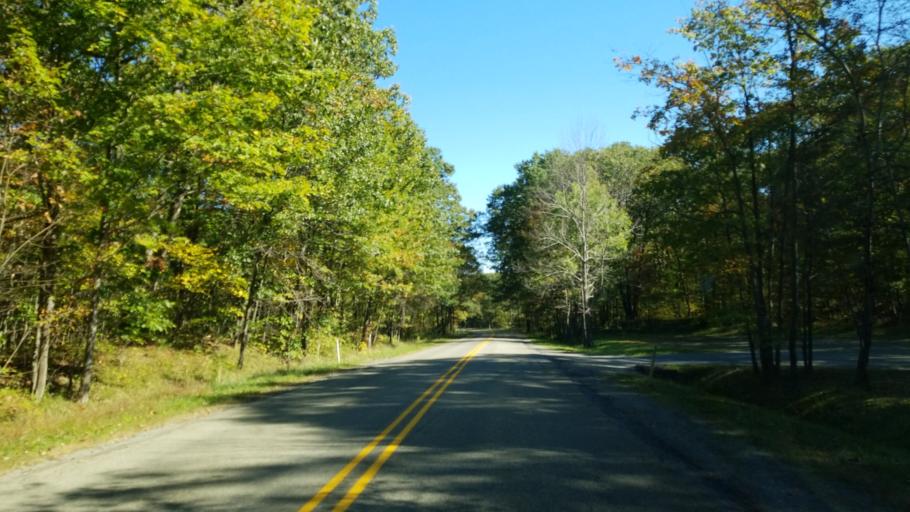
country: US
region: Pennsylvania
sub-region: Clearfield County
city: Shiloh
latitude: 41.2519
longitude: -78.3518
